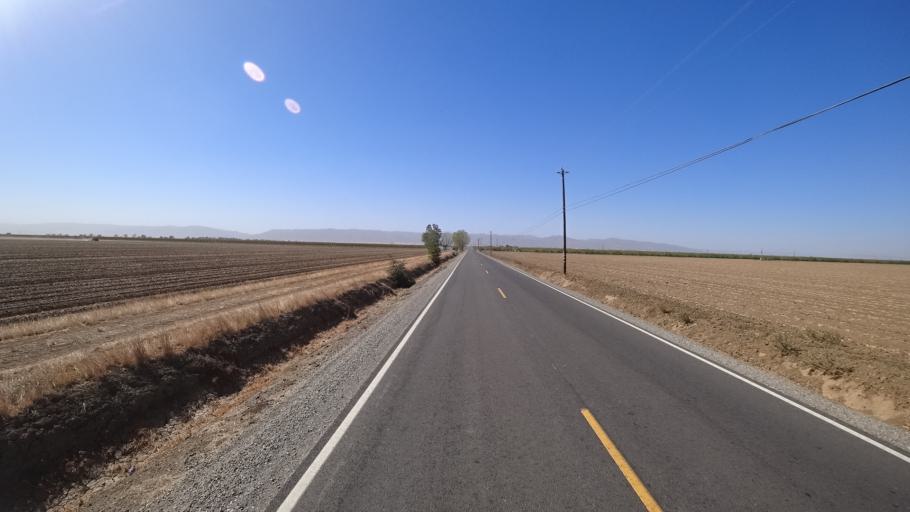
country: US
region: California
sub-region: Yolo County
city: Winters
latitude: 38.5839
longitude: -121.9400
